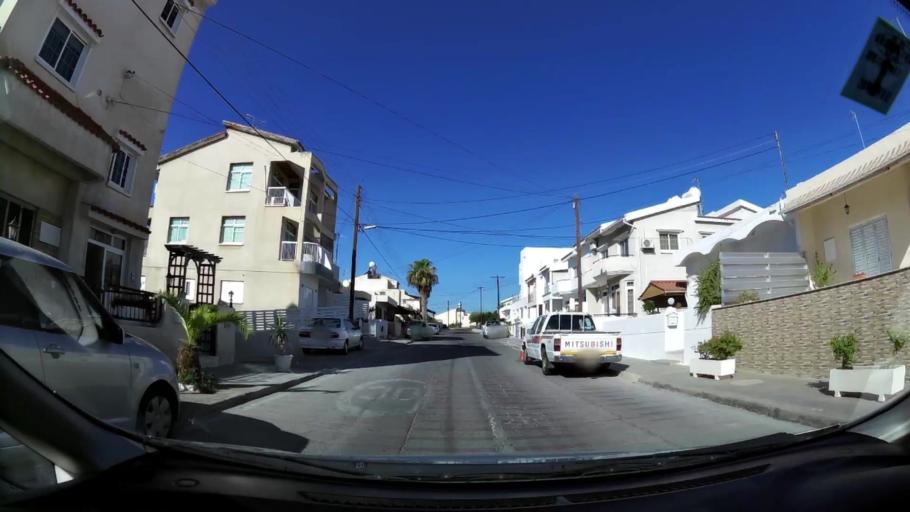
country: CY
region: Larnaka
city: Larnaca
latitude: 34.9302
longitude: 33.6084
